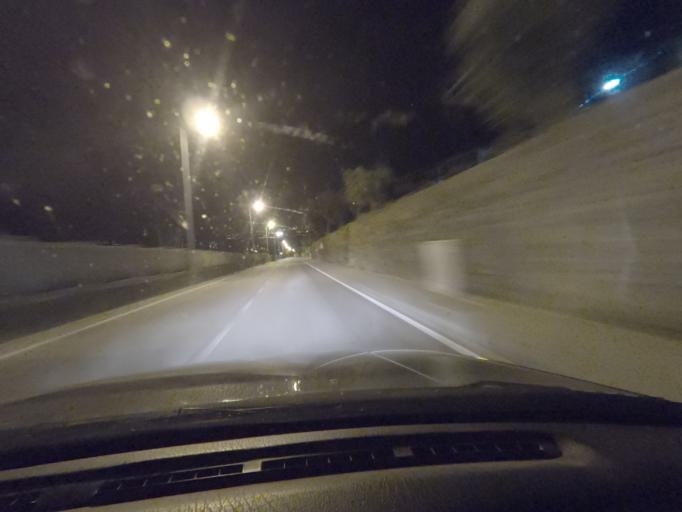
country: PT
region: Vila Real
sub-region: Peso da Regua
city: Godim
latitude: 41.1764
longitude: -7.7956
